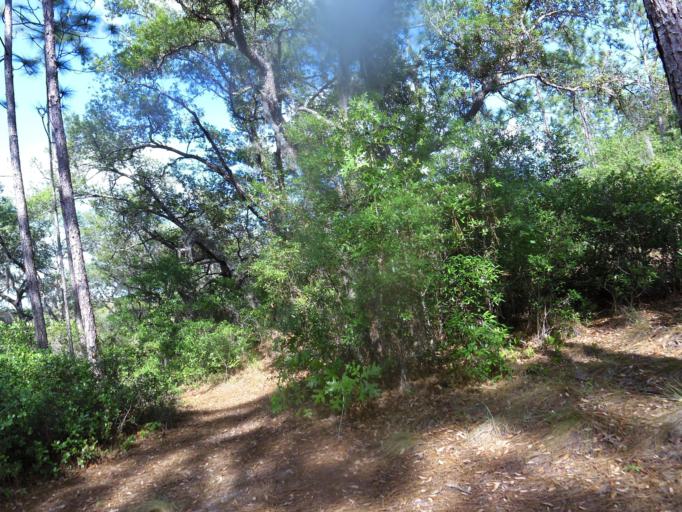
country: US
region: Florida
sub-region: Clay County
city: Keystone Heights
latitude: 29.8442
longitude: -81.9493
